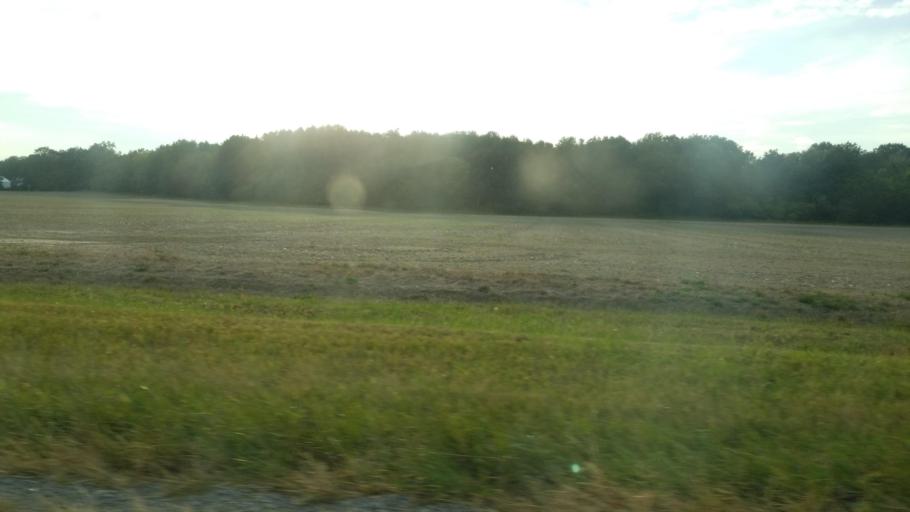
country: US
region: Illinois
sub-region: Saline County
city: Harrisburg
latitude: 37.7911
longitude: -88.5398
